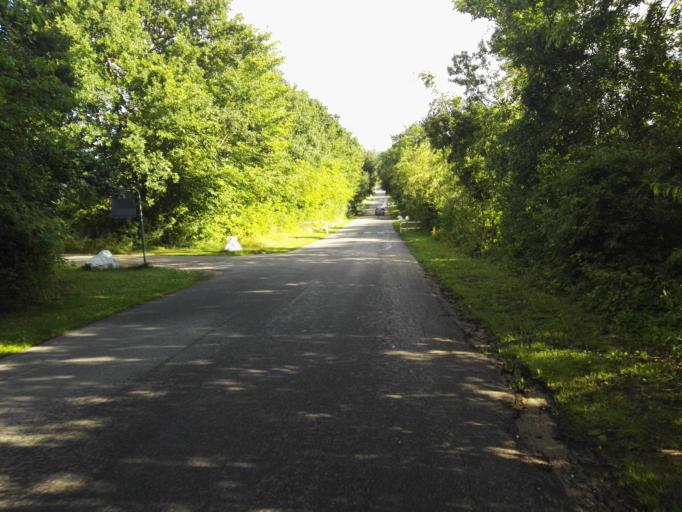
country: DK
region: Capital Region
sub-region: Ballerup Kommune
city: Ballerup
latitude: 55.7189
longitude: 12.3398
